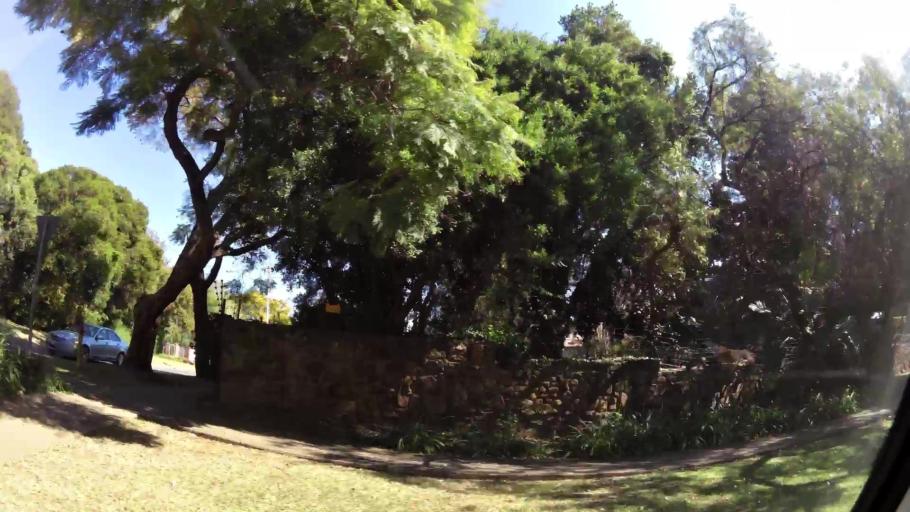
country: ZA
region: Gauteng
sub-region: City of Tshwane Metropolitan Municipality
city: Pretoria
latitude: -25.7770
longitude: 28.2489
